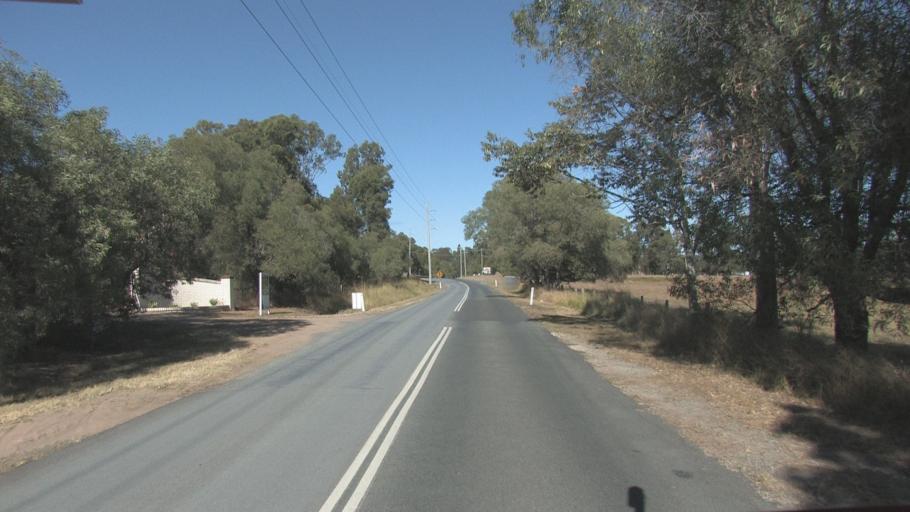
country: AU
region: Queensland
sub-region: Logan
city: Cedar Vale
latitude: -27.8660
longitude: 153.0178
